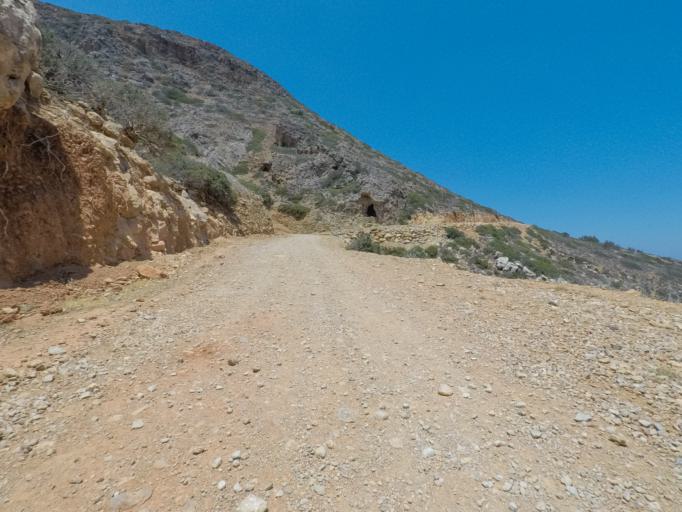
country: GR
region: Crete
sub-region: Nomos Lasithiou
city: Elounda
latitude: 35.3177
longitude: 25.7540
